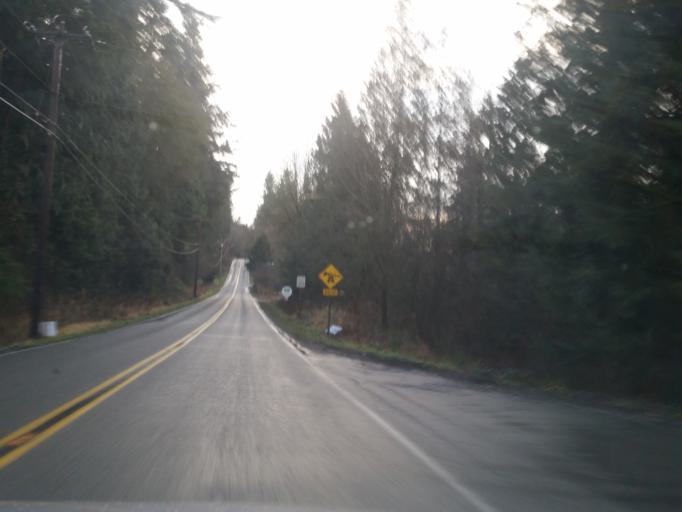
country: US
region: Washington
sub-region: Snohomish County
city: Cathcart
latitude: 47.8251
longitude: -122.0934
